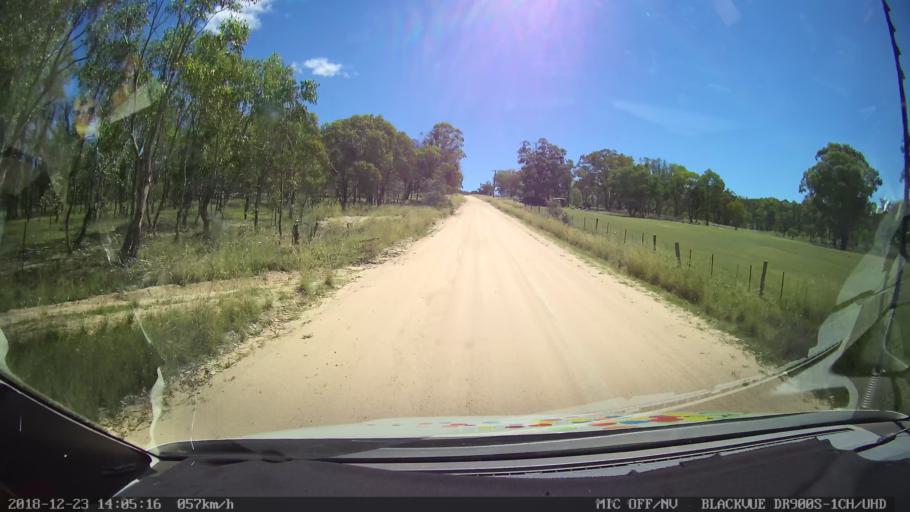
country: AU
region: New South Wales
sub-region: Tamworth Municipality
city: Manilla
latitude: -30.6243
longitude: 151.0821
